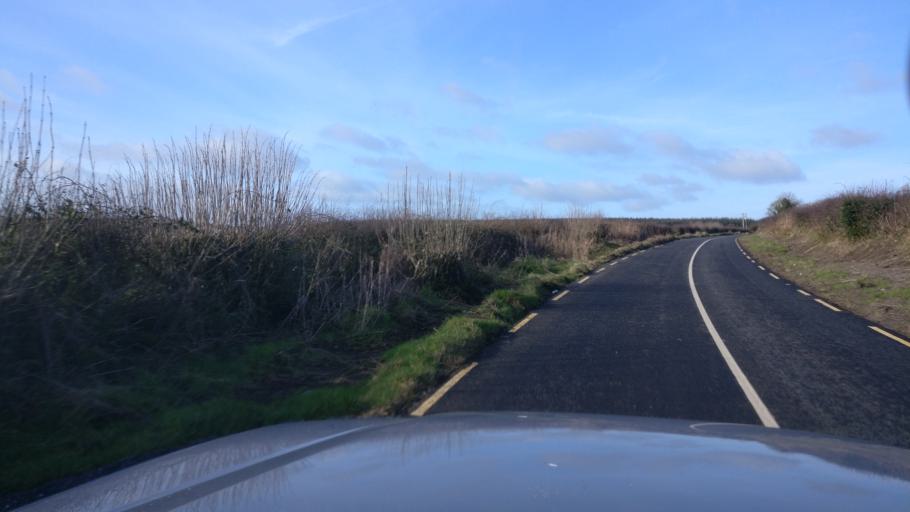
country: IE
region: Leinster
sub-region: Kilkenny
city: Castlecomer
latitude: 52.9046
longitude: -7.1812
